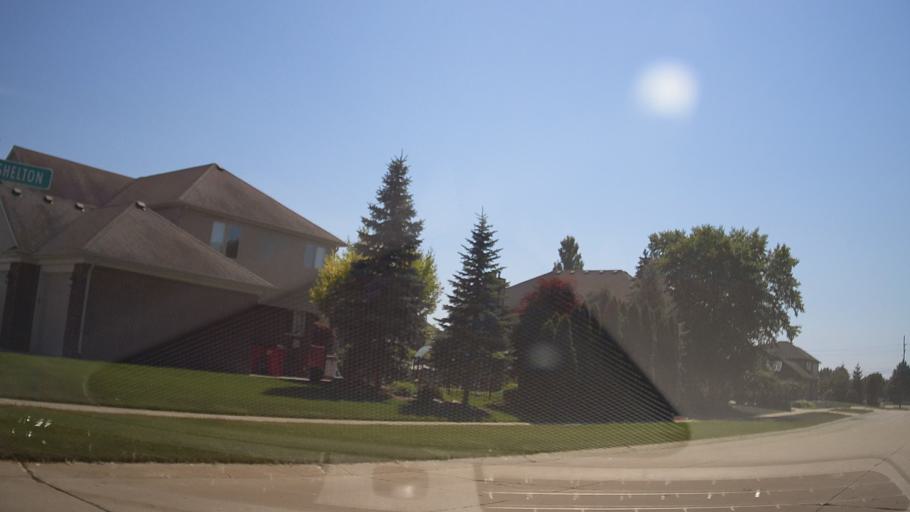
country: US
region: Michigan
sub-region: Macomb County
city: Clinton
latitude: 42.6513
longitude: -82.9150
